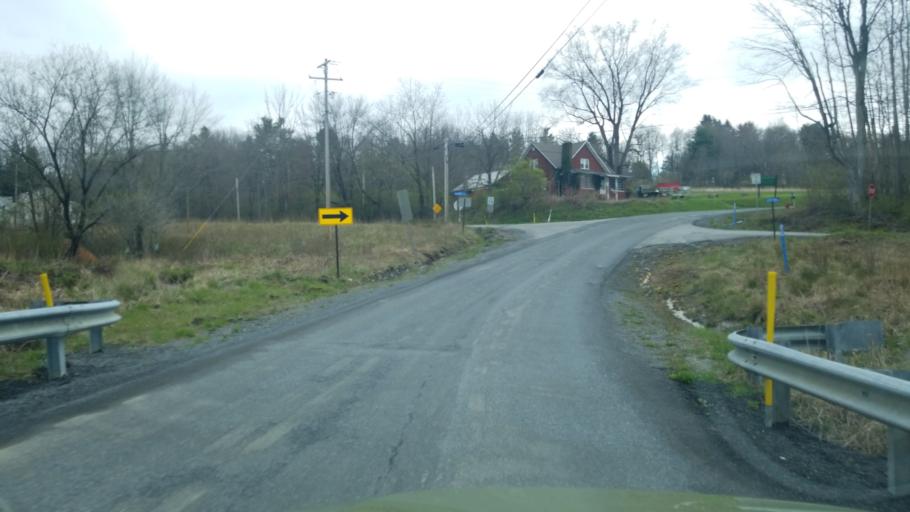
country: US
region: Pennsylvania
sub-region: Clearfield County
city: Clearfield
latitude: 41.0832
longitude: -78.4082
